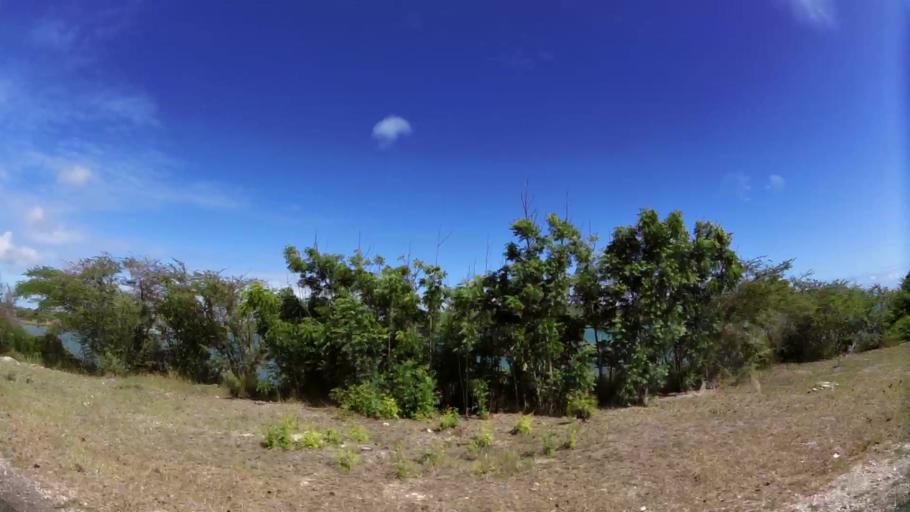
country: AG
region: Saint Paul
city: Falmouth
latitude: 17.0322
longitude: -61.7407
